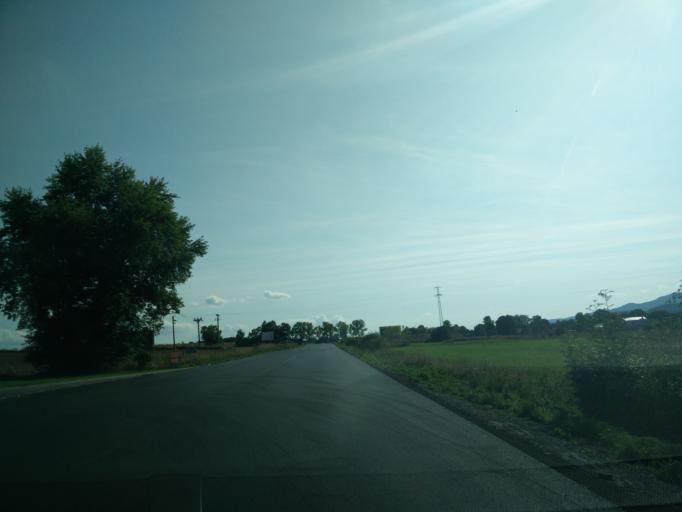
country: SK
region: Zilinsky
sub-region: Okres Martin
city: Martin
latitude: 49.0028
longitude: 18.8909
